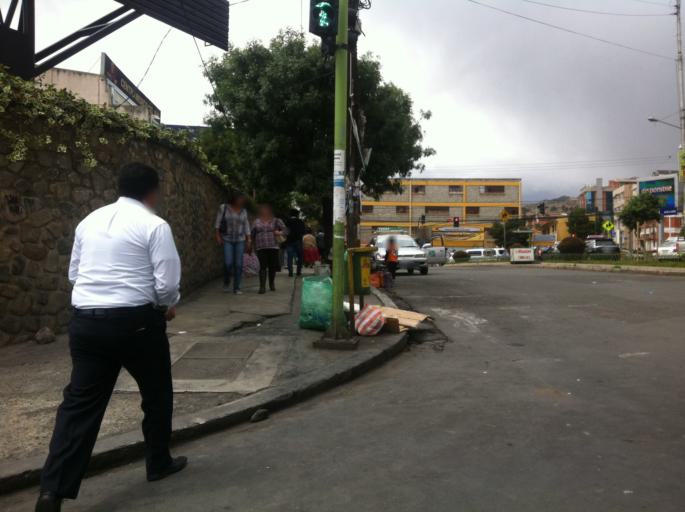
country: BO
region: La Paz
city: La Paz
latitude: -16.5396
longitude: -68.0780
